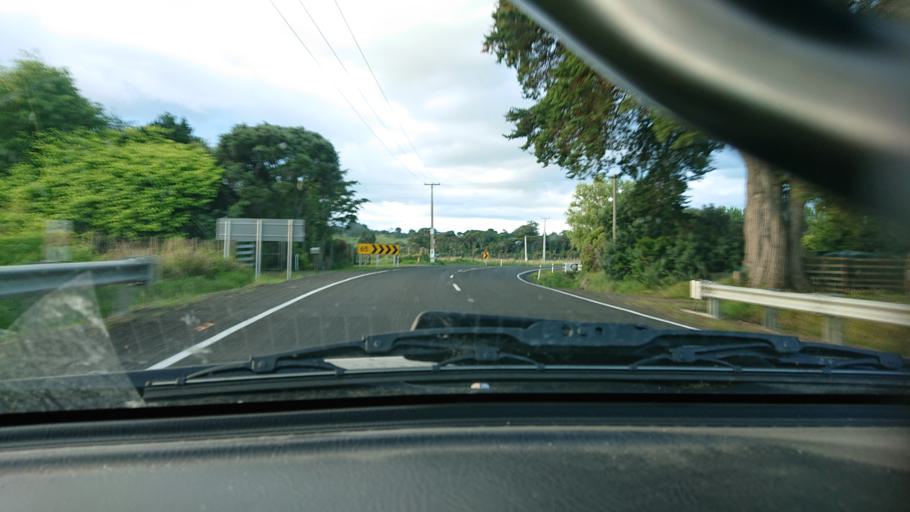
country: NZ
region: Auckland
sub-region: Auckland
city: Parakai
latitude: -36.4961
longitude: 174.4488
